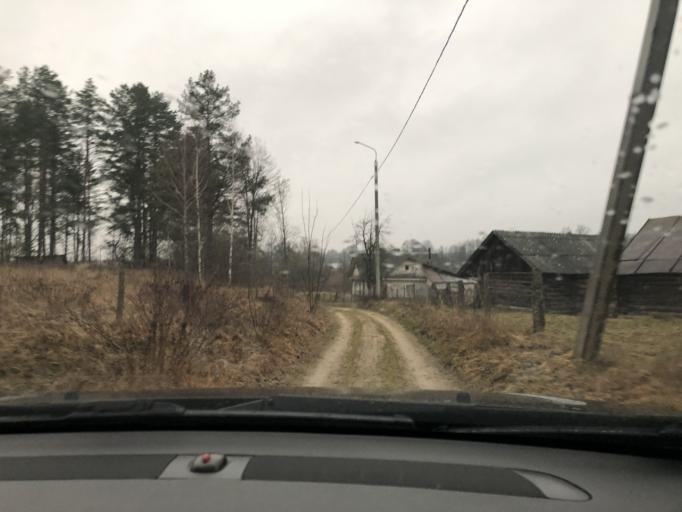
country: LT
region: Alytaus apskritis
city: Druskininkai
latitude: 53.9065
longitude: 24.1785
